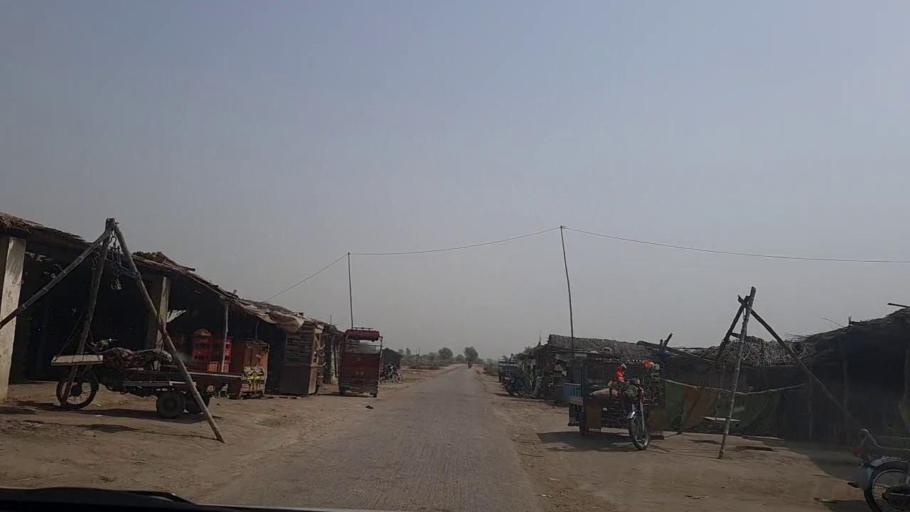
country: PK
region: Sindh
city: Pithoro
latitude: 25.4890
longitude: 69.2150
